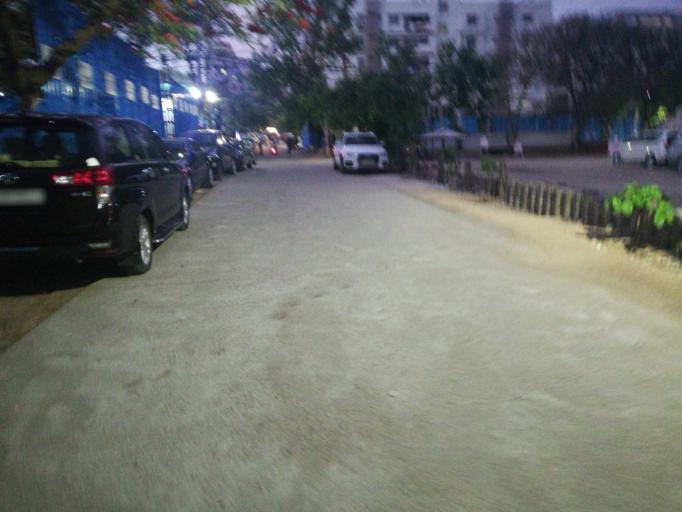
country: IN
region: Telangana
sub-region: Rangareddi
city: Kukatpalli
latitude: 17.4610
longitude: 78.3683
